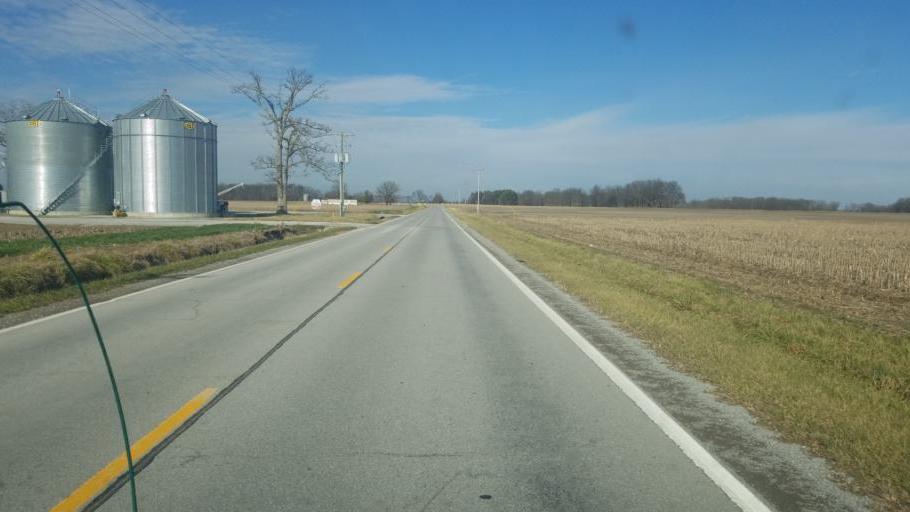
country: US
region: Illinois
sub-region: Saline County
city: Eldorado
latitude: 37.9023
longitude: -88.4530
